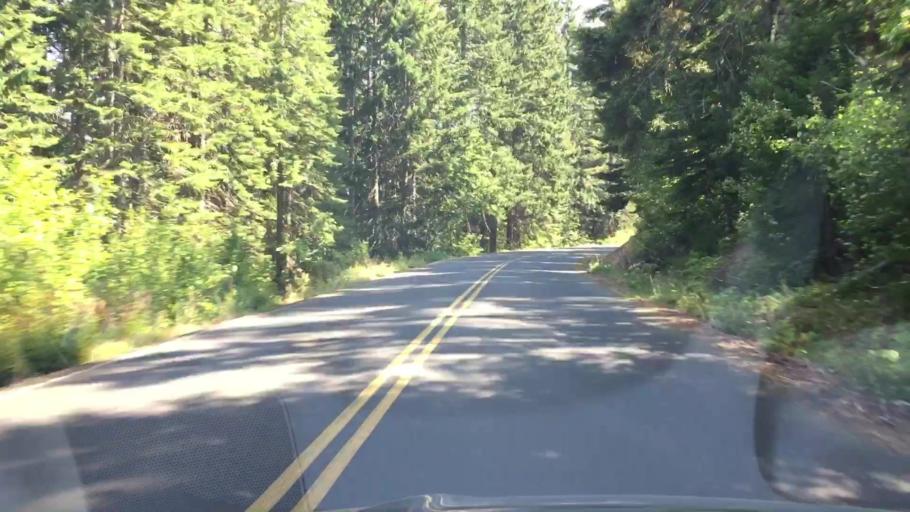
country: US
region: Washington
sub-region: Klickitat County
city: White Salmon
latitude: 46.0502
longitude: -121.5558
